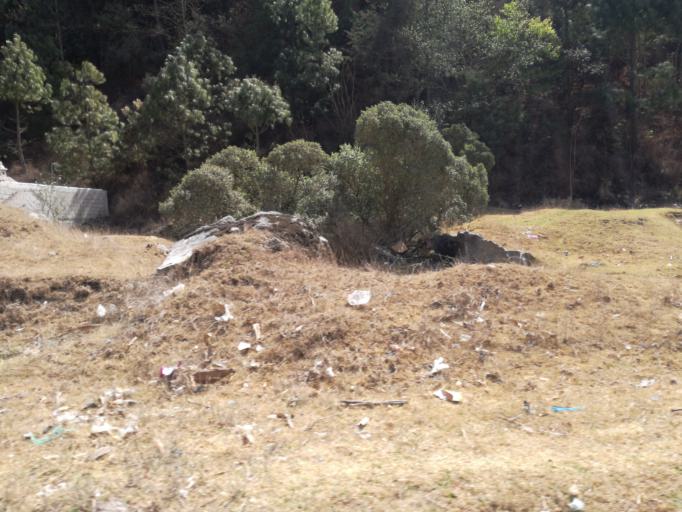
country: GT
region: Quetzaltenango
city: Almolonga
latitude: 14.7894
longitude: -91.5372
